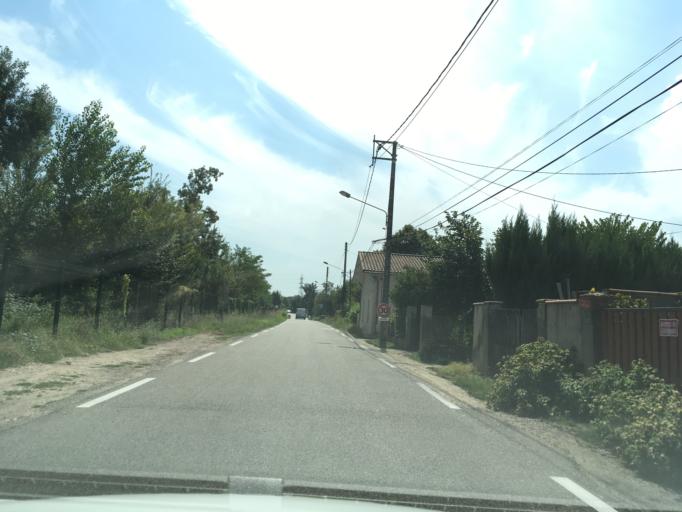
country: FR
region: Midi-Pyrenees
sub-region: Departement du Tarn-et-Garonne
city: Montauban
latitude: 44.0142
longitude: 1.3394
